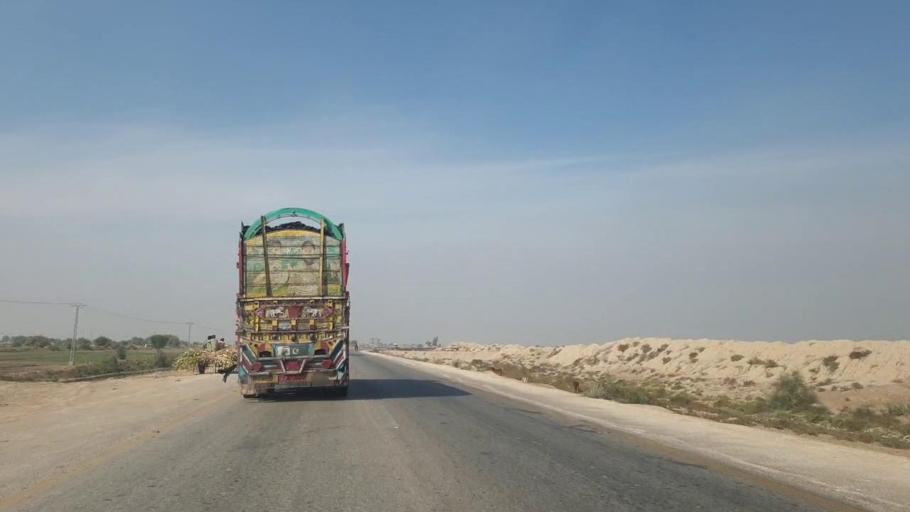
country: PK
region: Sindh
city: Sann
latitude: 25.9533
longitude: 68.1956
